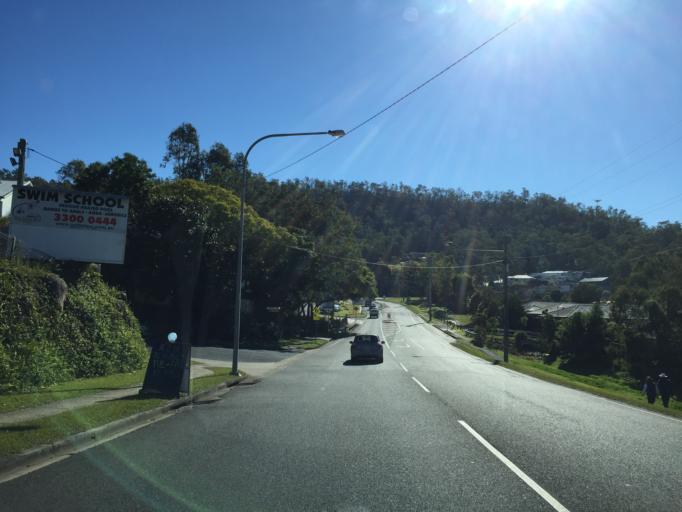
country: AU
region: Queensland
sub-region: Moreton Bay
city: Ferny Hills
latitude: -27.4321
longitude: 152.9428
